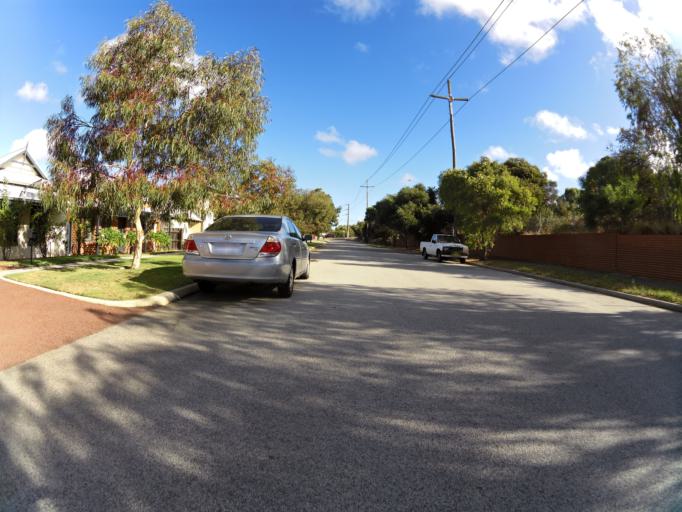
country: AU
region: Western Australia
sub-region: Fremantle
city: Fremantle
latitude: -32.0458
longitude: 115.7644
